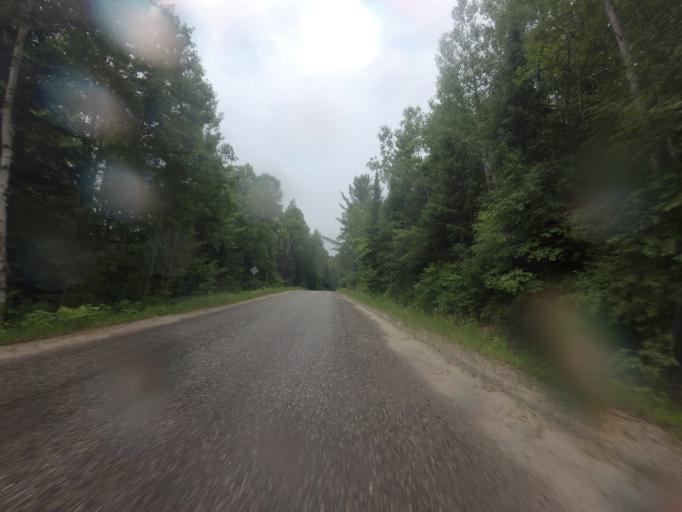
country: CA
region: Quebec
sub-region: Outaouais
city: Maniwaki
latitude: 46.4337
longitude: -75.9451
